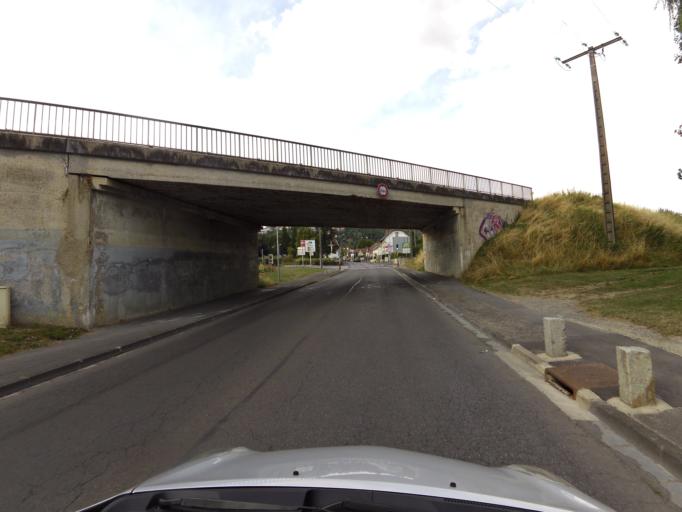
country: FR
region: Picardie
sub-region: Departement de l'Aisne
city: Laon
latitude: 49.5541
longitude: 3.6288
